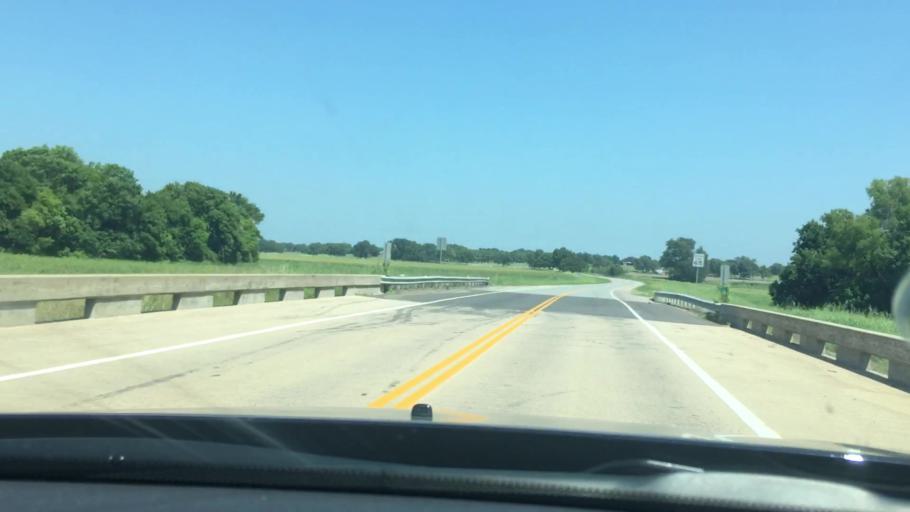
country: US
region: Oklahoma
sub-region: Johnston County
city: Tishomingo
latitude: 34.2510
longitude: -96.5494
